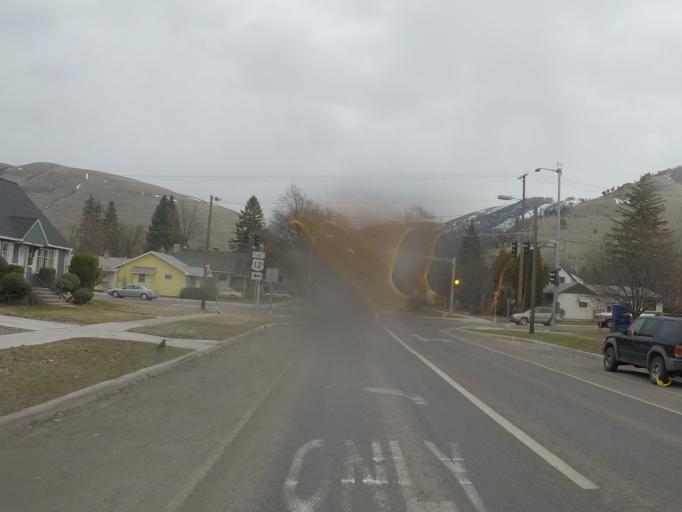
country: US
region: Montana
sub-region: Missoula County
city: Missoula
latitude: 46.8641
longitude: -113.9900
